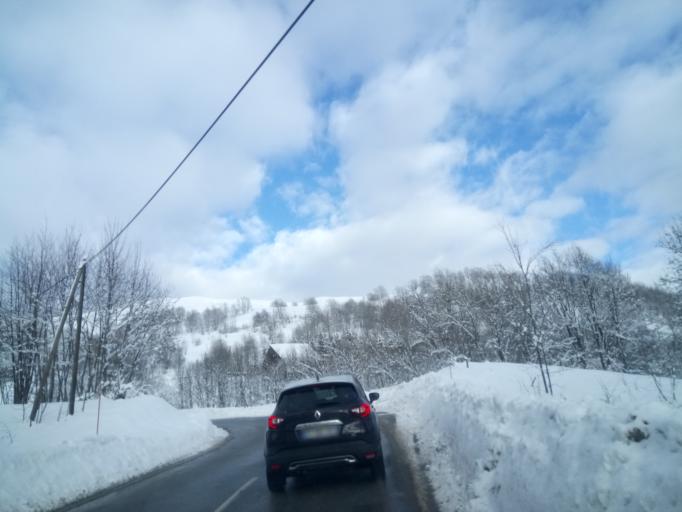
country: FR
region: Rhone-Alpes
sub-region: Departement de la Savoie
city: Saint-Jean-de-Maurienne
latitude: 45.2539
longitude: 6.2915
